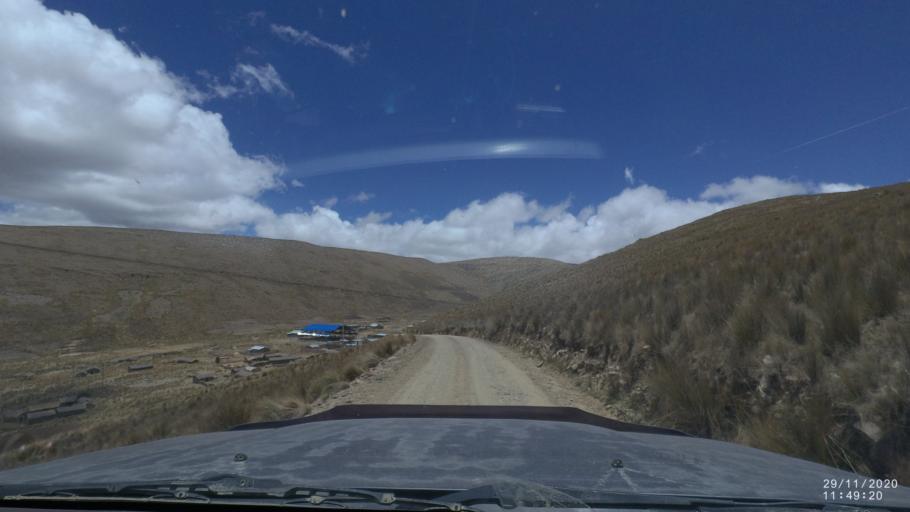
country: BO
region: Cochabamba
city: Cochabamba
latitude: -17.1765
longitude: -66.2600
